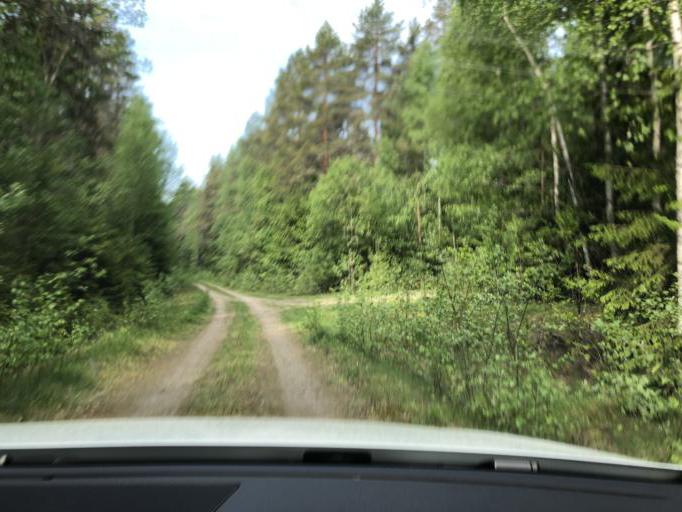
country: SE
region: Dalarna
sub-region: Avesta Kommun
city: Horndal
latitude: 60.2167
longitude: 16.5046
